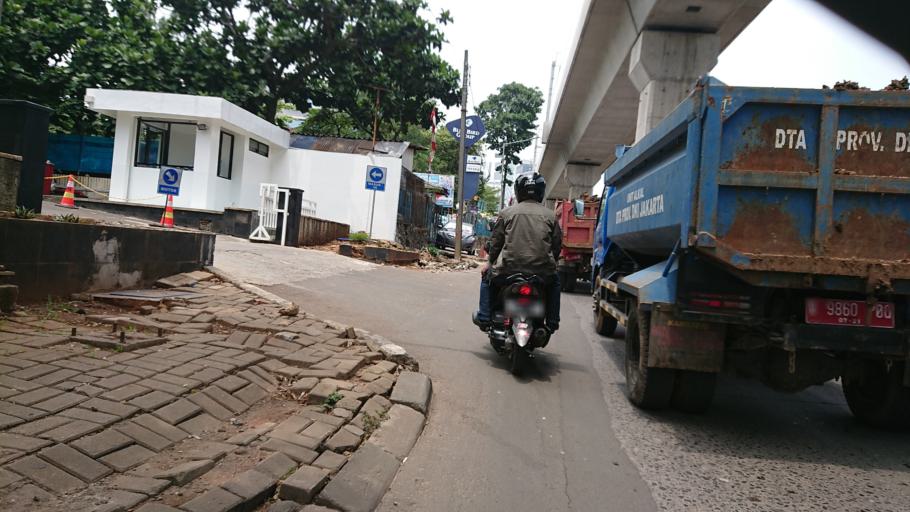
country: ID
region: Banten
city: South Tangerang
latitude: -6.2918
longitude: 106.7837
